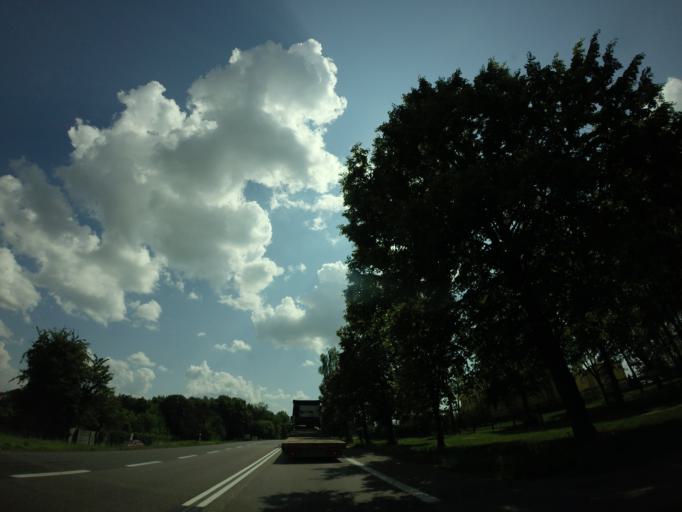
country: PL
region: Podlasie
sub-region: Powiat lomzynski
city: Piatnica
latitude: 53.2103
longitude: 22.1039
